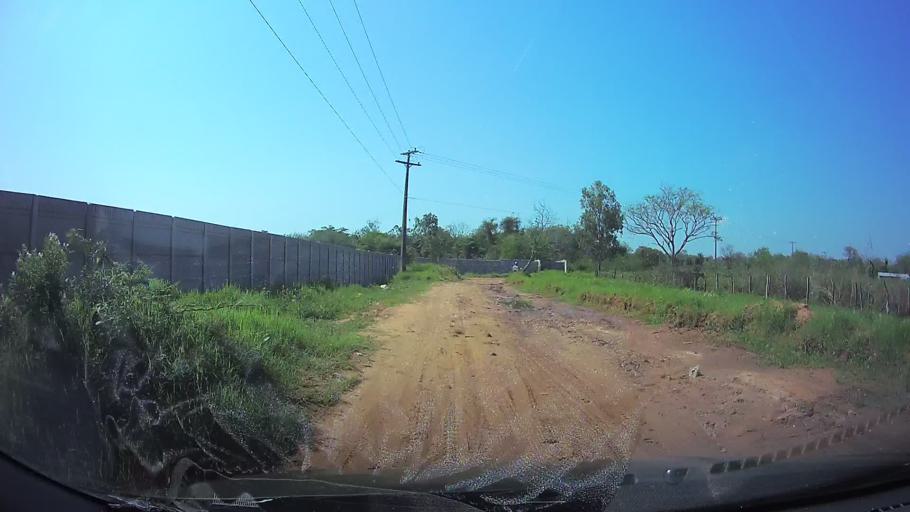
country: PY
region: Central
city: Limpio
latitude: -25.2140
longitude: -57.4835
